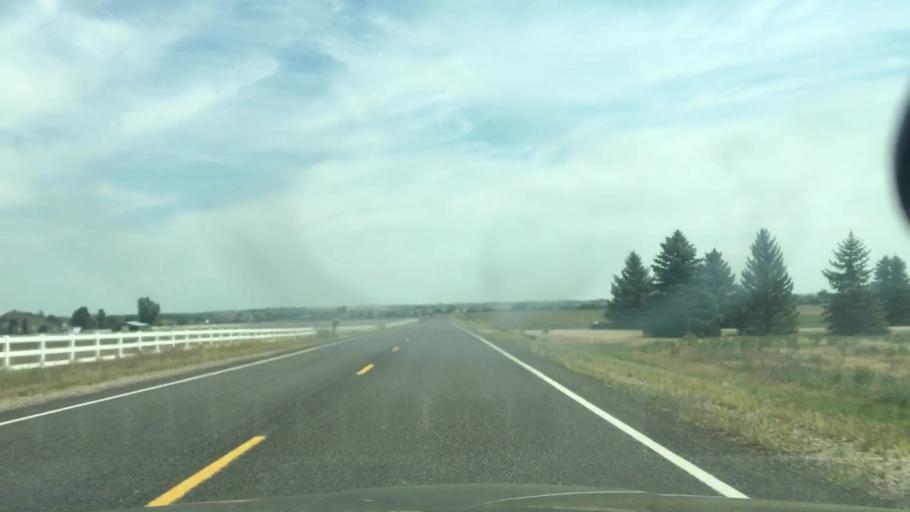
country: US
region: Colorado
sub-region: Larimer County
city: Berthoud
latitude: 40.3340
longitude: -105.1566
